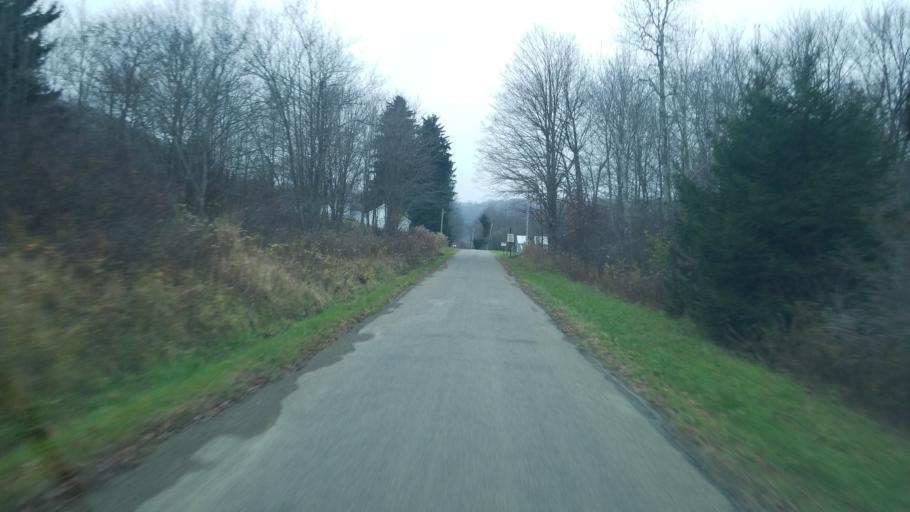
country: US
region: Pennsylvania
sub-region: McKean County
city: Smethport
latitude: 41.7830
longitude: -78.4382
